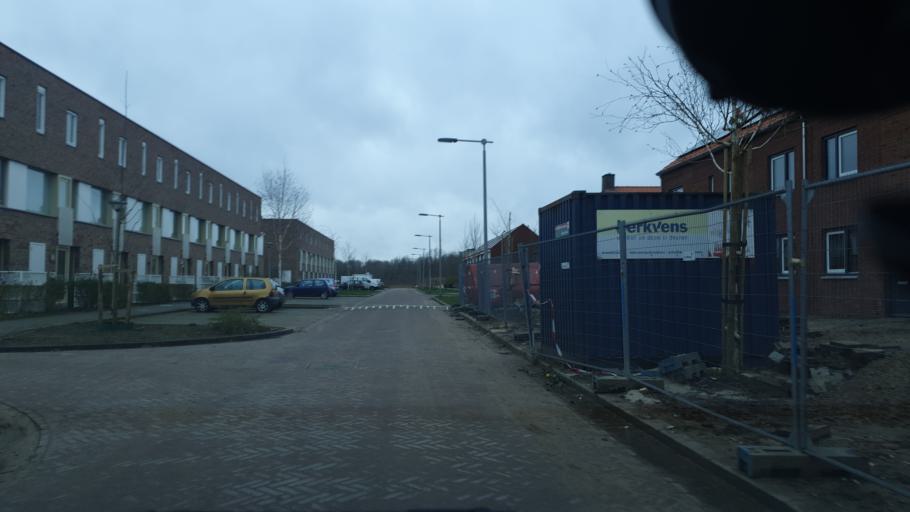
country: NL
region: Gelderland
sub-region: Gemeente Arnhem
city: Arnhem
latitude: 51.9611
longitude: 5.9183
